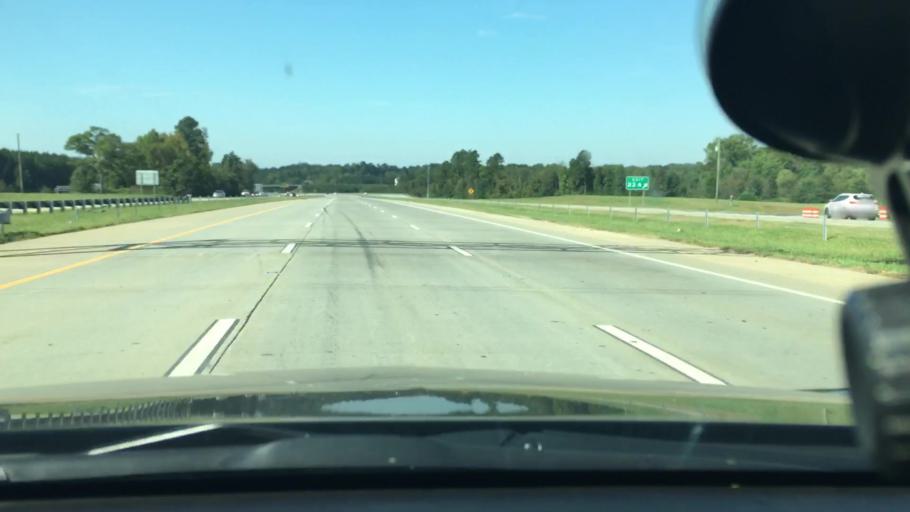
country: US
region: North Carolina
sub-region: Mecklenburg County
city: Huntersville
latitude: 35.3637
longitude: -80.8436
